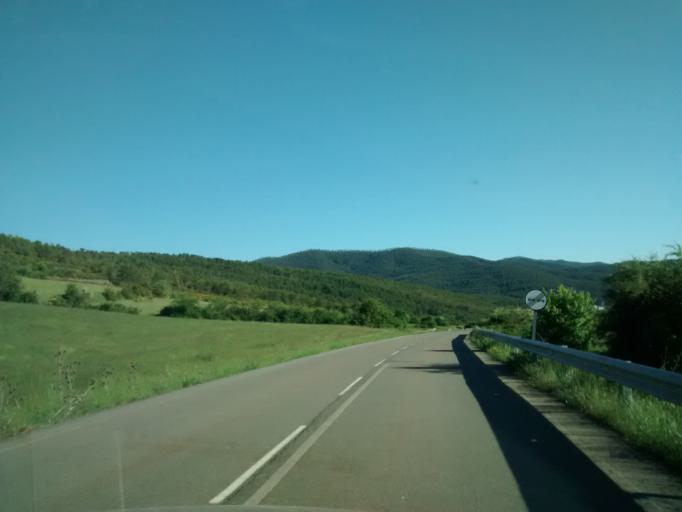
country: ES
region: Aragon
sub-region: Provincia de Huesca
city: Borau
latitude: 42.6733
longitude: -0.6207
